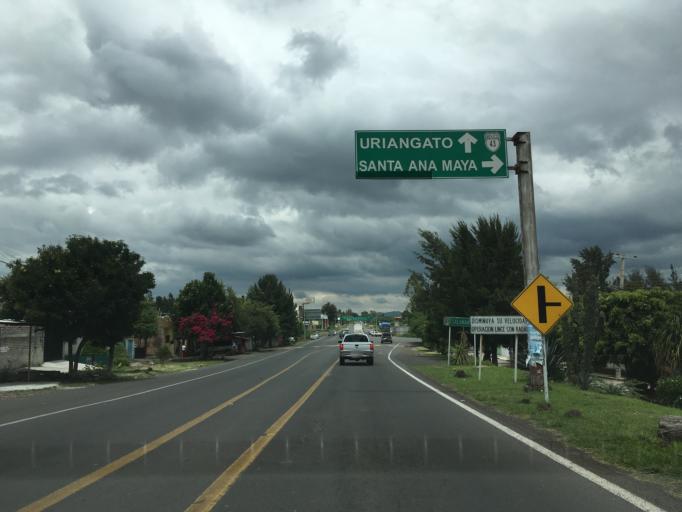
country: MX
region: Guanajuato
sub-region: Moroleon
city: Rinconadas del Bosque
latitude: 20.0854
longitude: -101.1563
